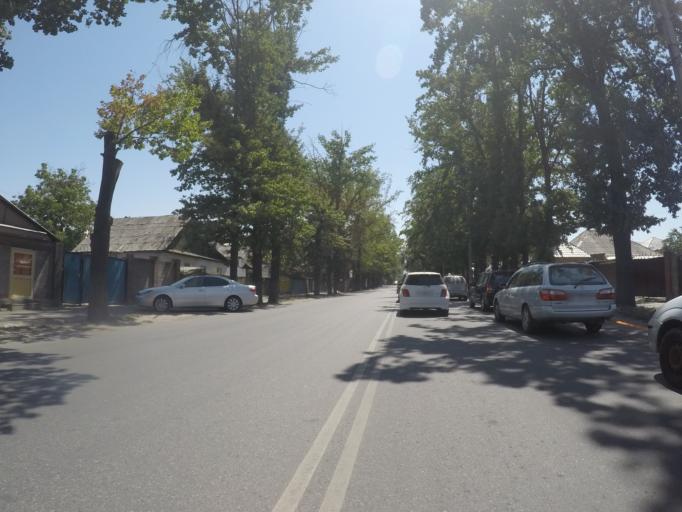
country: KG
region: Chuy
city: Bishkek
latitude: 42.8532
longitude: 74.5770
